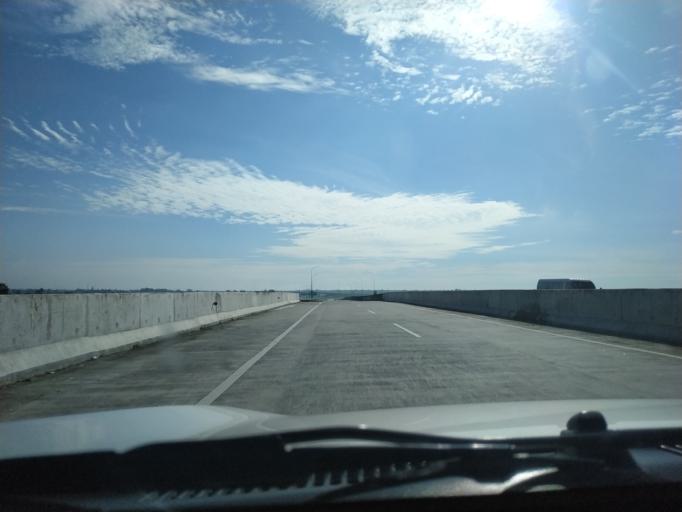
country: ID
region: North Sumatra
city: Perbaungan
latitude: 3.5317
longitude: 98.8864
